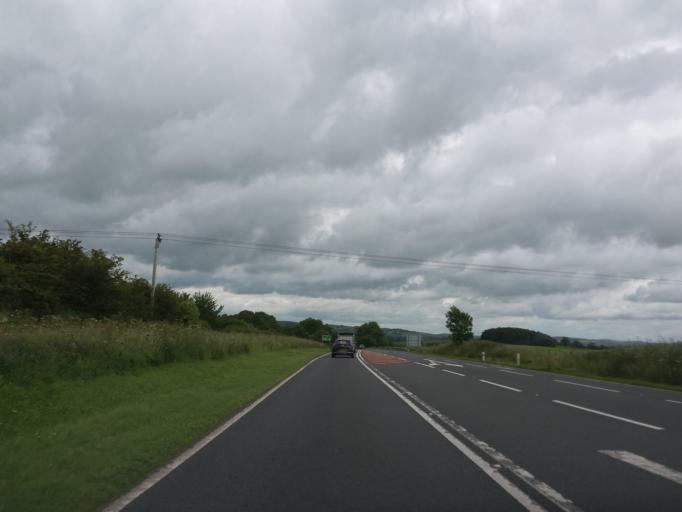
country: GB
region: Scotland
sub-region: Dumfries and Galloway
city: Castle Douglas
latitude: 54.9642
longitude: -3.9075
